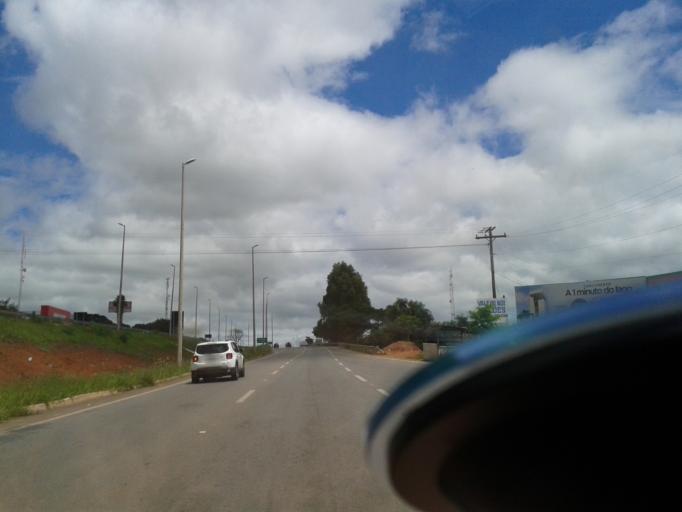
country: BR
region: Goias
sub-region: Inhumas
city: Inhumas
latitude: -16.3888
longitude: -49.4959
